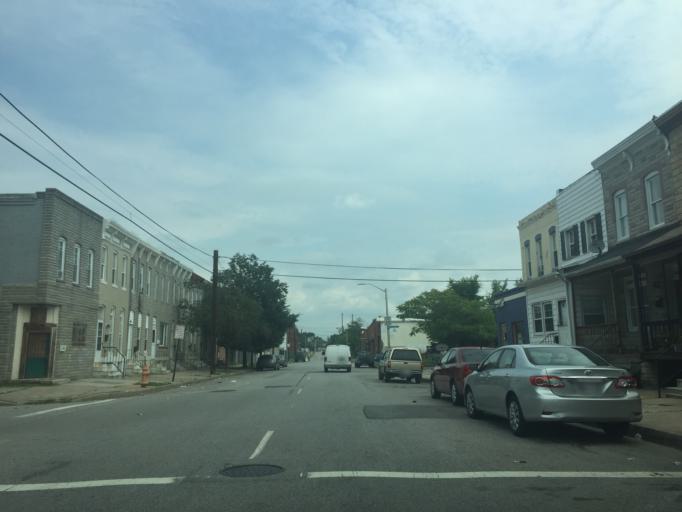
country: US
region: Maryland
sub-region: Baltimore County
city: Rosedale
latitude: 39.2938
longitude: -76.5600
